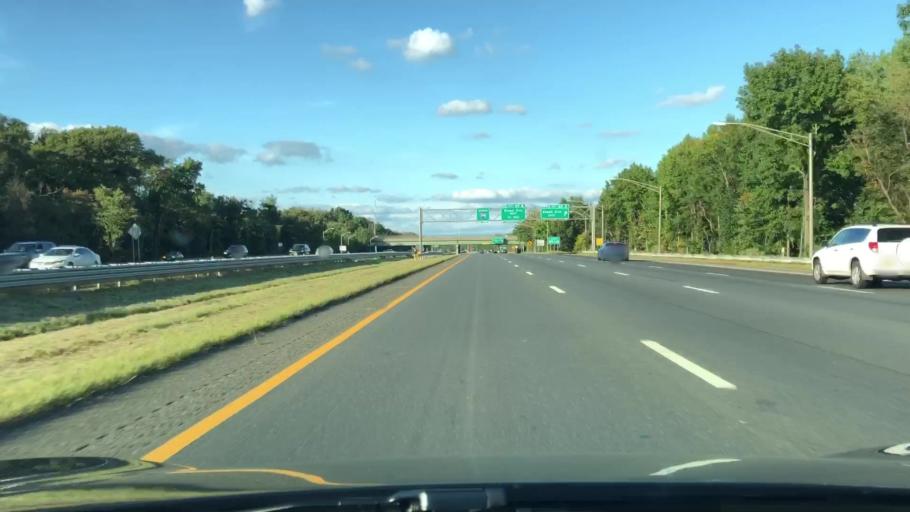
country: US
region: New Jersey
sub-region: Mercer County
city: Mercerville
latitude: 40.2480
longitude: -74.6985
